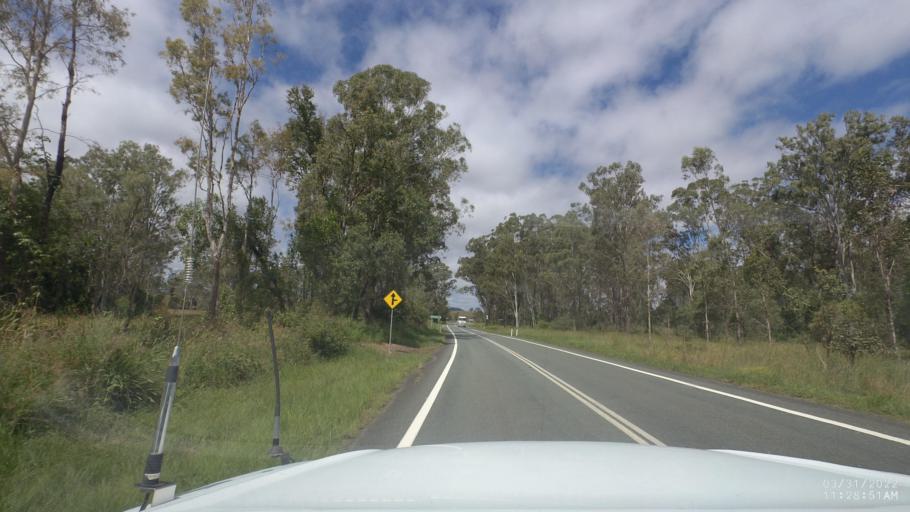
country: AU
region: Queensland
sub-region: Logan
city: Cedar Vale
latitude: -27.9307
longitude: 153.0796
